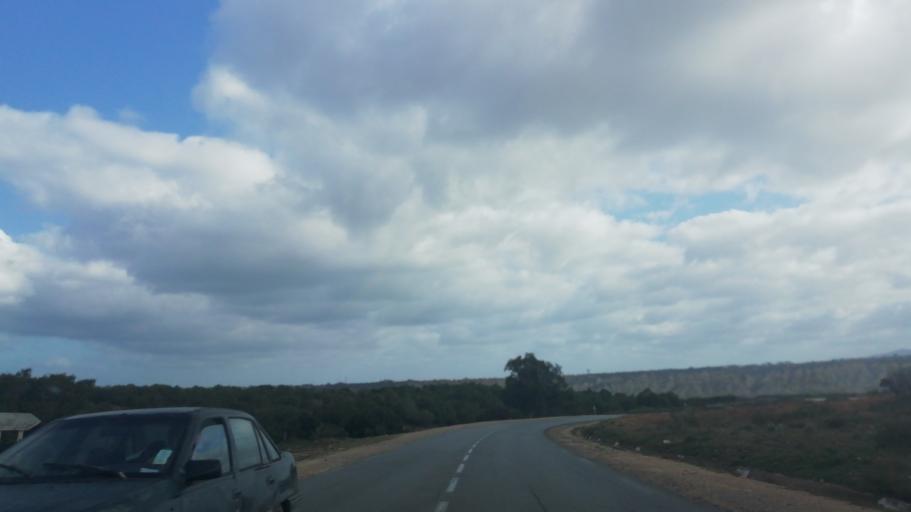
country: DZ
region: Relizane
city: Mazouna
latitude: 36.2908
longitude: 0.6518
